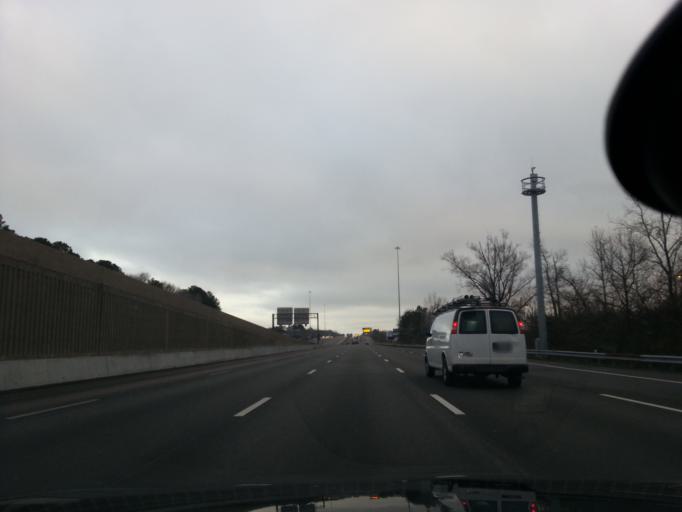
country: US
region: Virginia
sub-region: City of Chesapeake
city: Chesapeake
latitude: 36.8501
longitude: -76.1959
